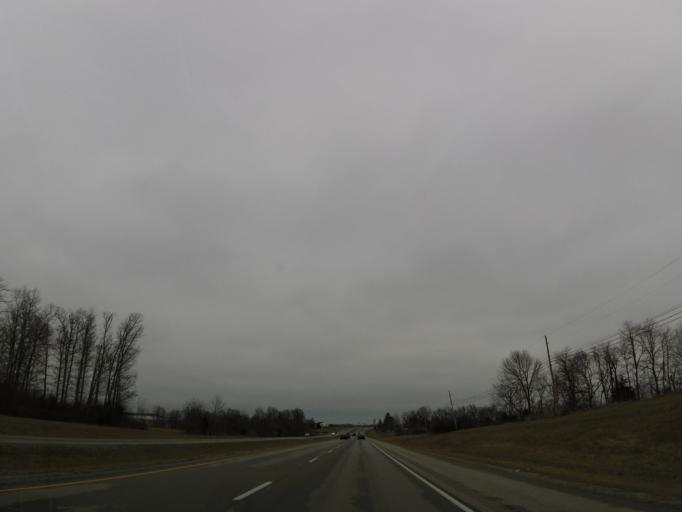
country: US
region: Kentucky
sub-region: Anderson County
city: Lawrenceburg
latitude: 38.1189
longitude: -84.9150
